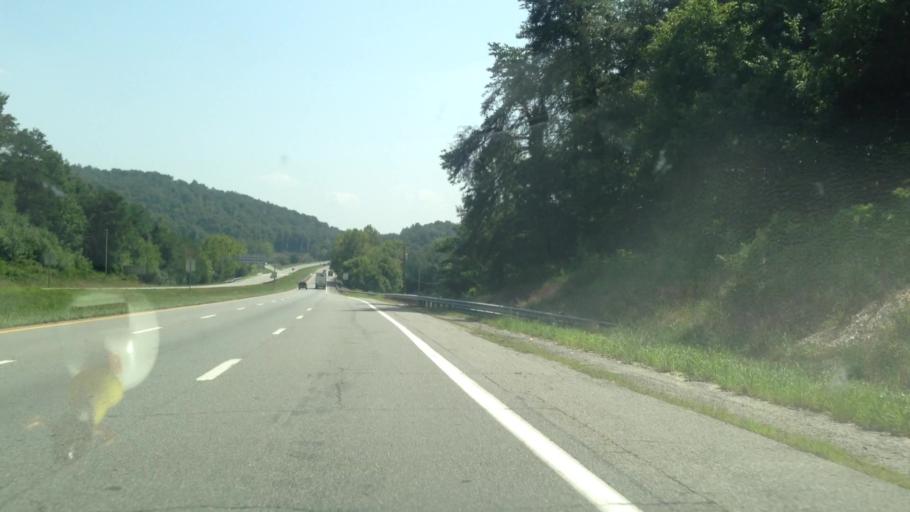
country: US
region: Virginia
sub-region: Henry County
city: Stanleytown
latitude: 36.7343
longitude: -79.9376
